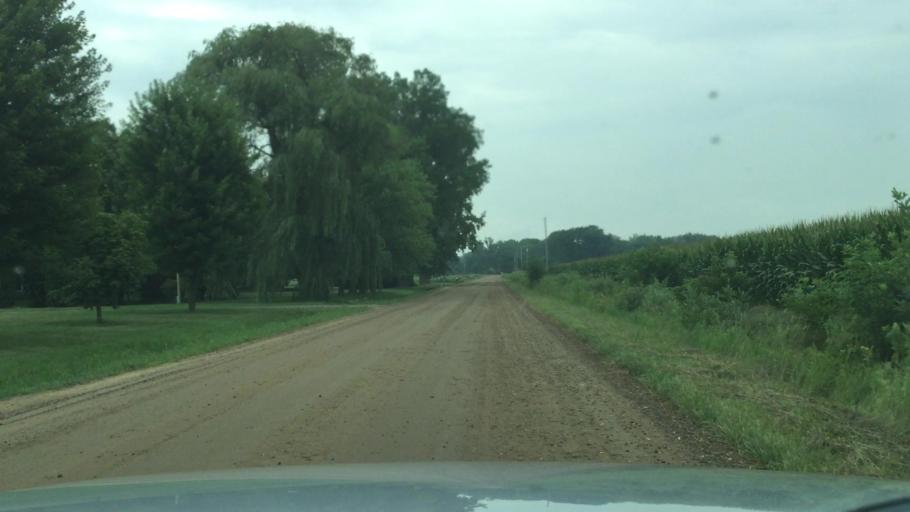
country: US
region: Michigan
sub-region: Shiawassee County
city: Durand
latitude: 42.9407
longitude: -83.9376
